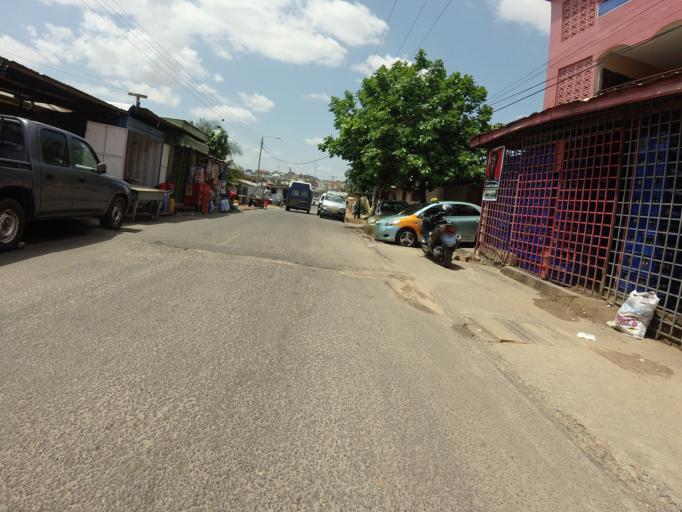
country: GH
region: Greater Accra
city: Accra
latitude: 5.5789
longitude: -0.2012
